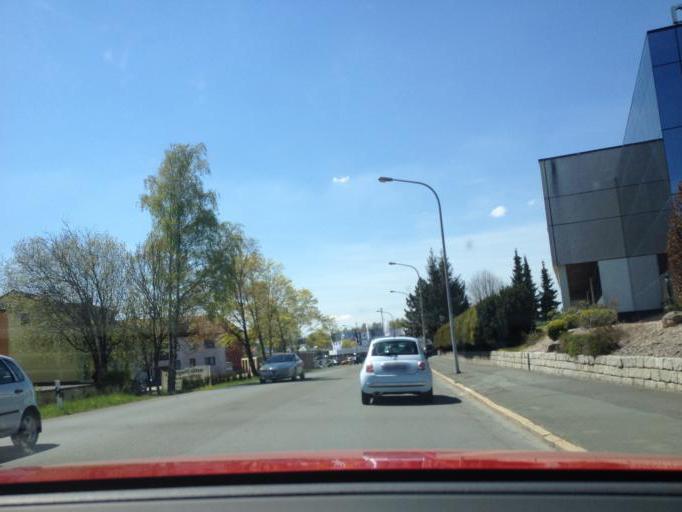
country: DE
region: Bavaria
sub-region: Upper Franconia
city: Dohlau
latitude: 50.2911
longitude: 11.9273
